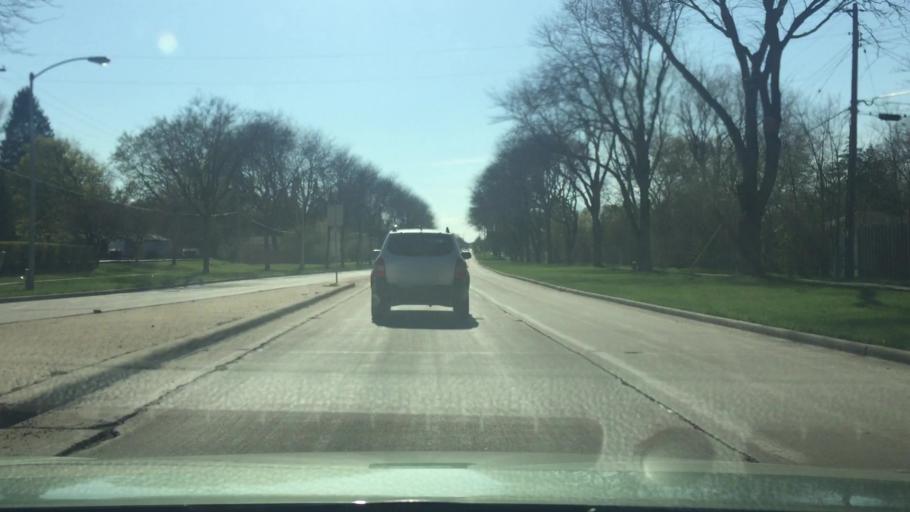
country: US
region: Wisconsin
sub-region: Milwaukee County
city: Brown Deer
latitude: 43.1632
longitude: -87.9759
